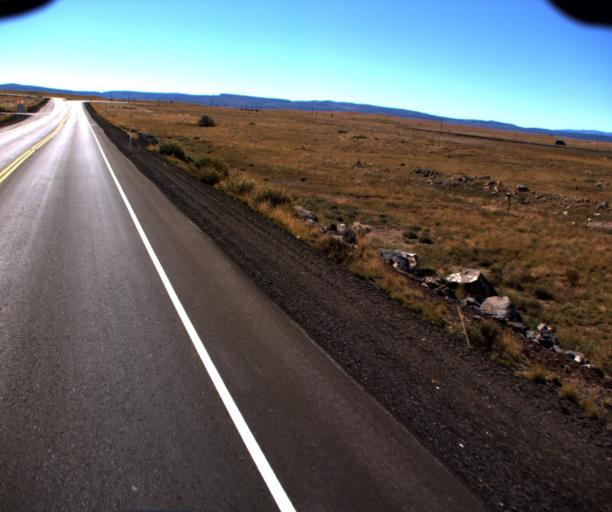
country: US
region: Arizona
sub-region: Apache County
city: Springerville
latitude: 34.1784
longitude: -109.3182
